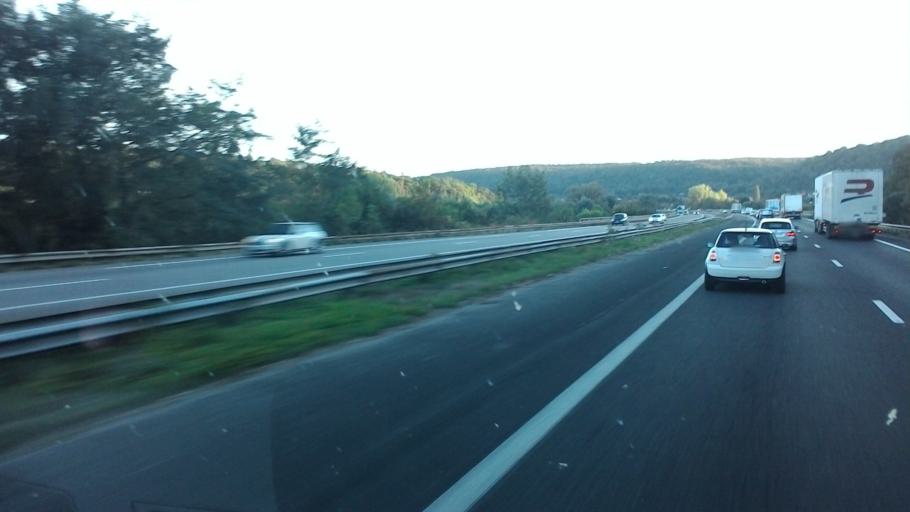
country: FR
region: Lorraine
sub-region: Departement de Meurthe-et-Moselle
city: Belleville
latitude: 48.8075
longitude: 6.1135
